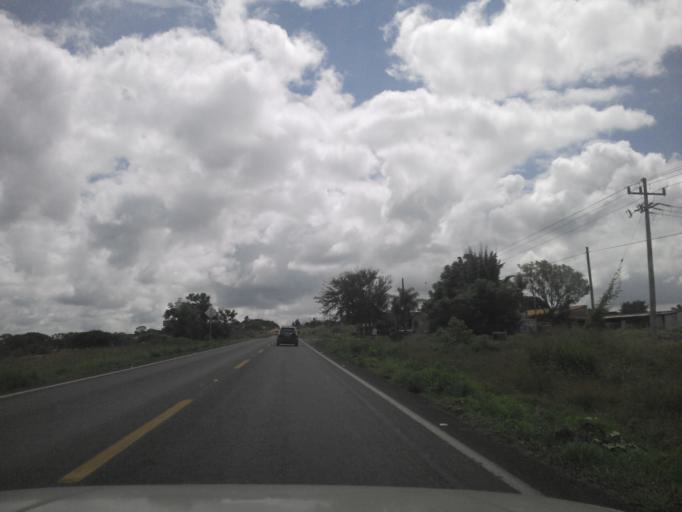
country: MX
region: Jalisco
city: Zapotlanejo
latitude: 20.6104
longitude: -102.9912
